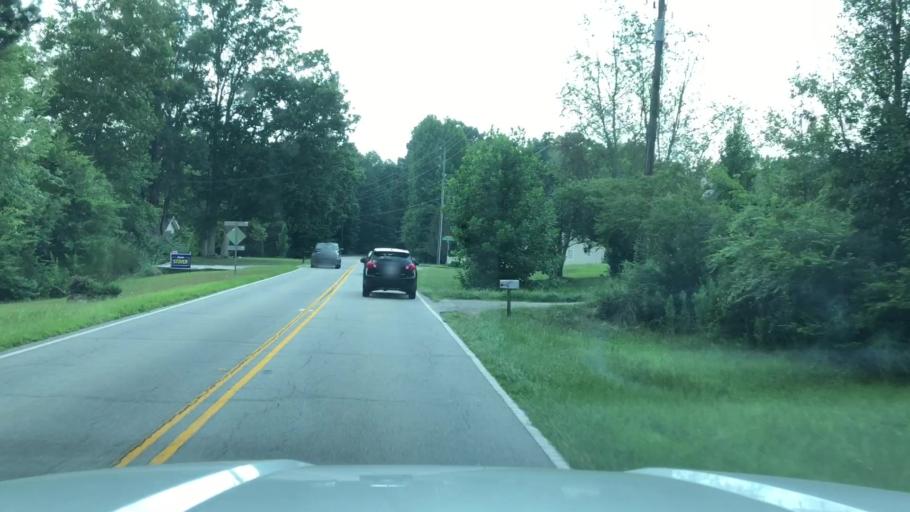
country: US
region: Georgia
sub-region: Paulding County
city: Dallas
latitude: 33.9725
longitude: -84.8097
